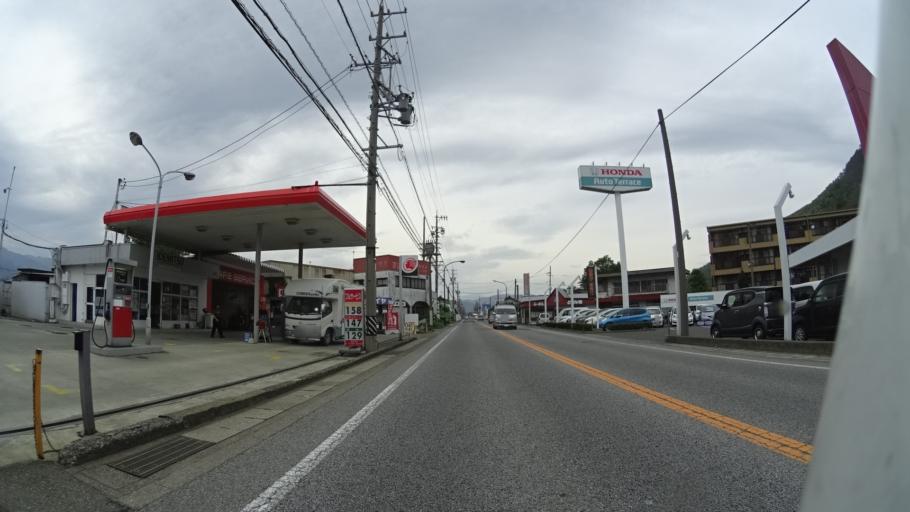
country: JP
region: Nagano
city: Nagano-shi
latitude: 36.5148
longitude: 138.1334
